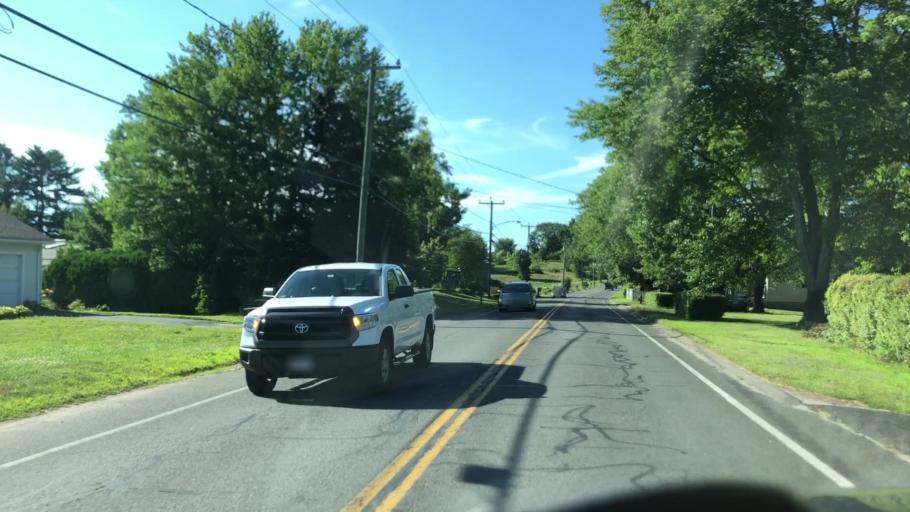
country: US
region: Massachusetts
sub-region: Hampshire County
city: Easthampton
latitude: 42.2841
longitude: -72.6705
